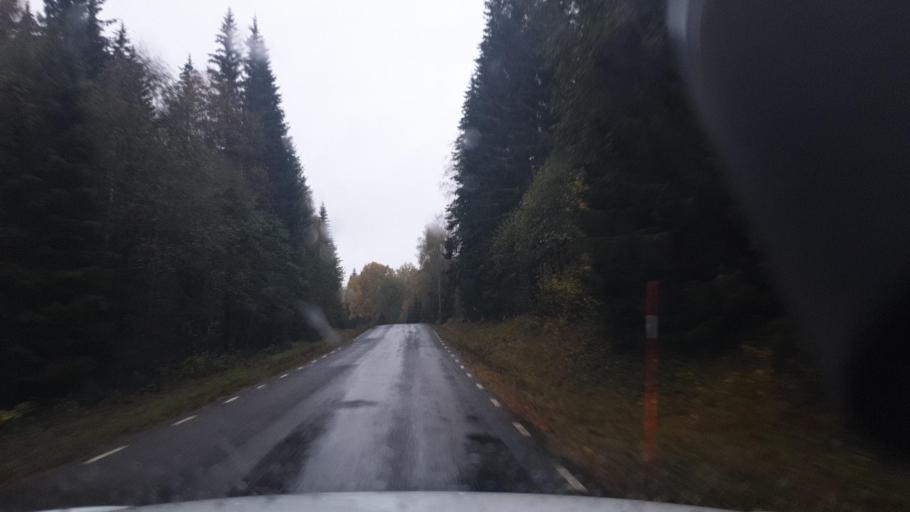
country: SE
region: Vaermland
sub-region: Eda Kommun
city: Amotfors
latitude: 59.8455
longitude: 12.4260
